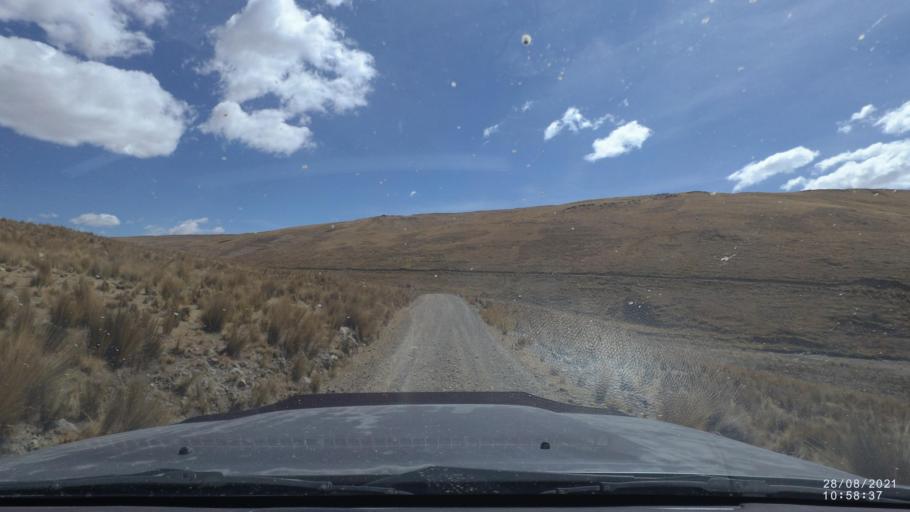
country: BO
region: Cochabamba
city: Cochabamba
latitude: -17.1844
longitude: -66.2540
